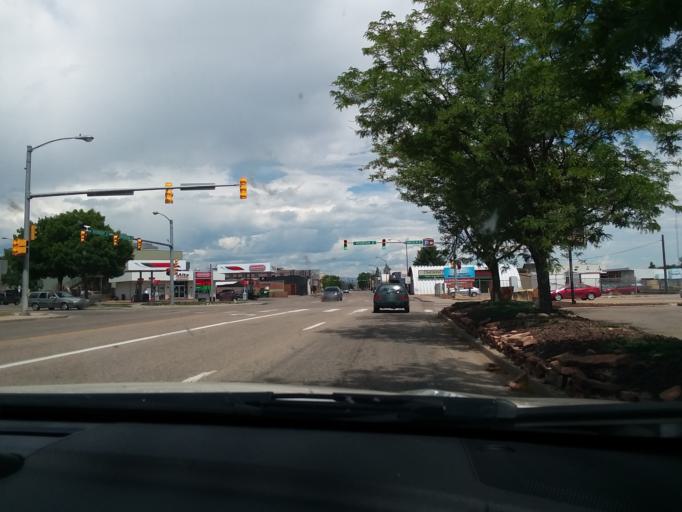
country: US
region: Colorado
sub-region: Larimer County
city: Fort Collins
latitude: 40.5869
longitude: -105.0711
